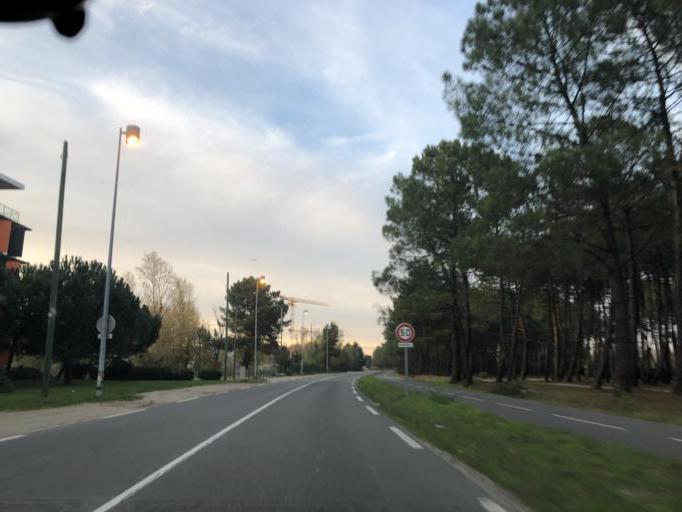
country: FR
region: Aquitaine
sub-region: Departement de la Gironde
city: Le Bouscat
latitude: 44.8804
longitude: -0.5836
